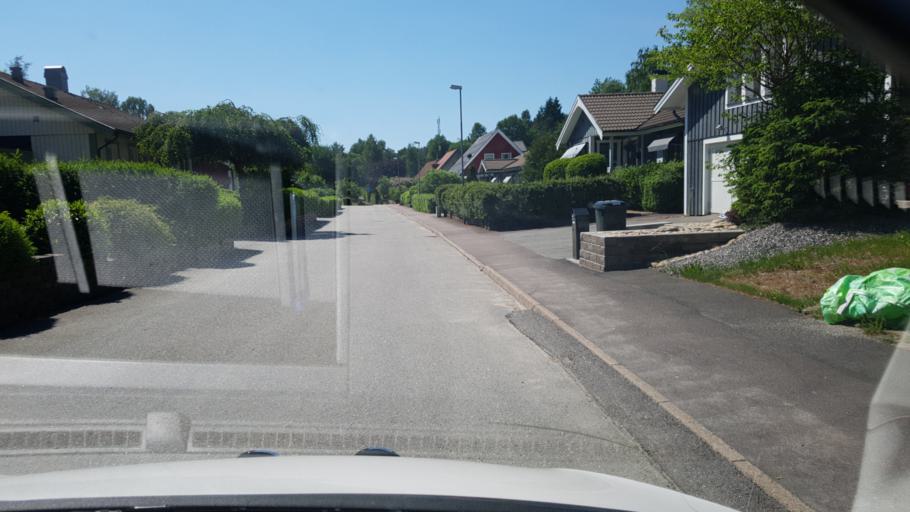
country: SE
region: Vaestra Goetaland
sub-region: Lerums Kommun
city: Stenkullen
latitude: 57.8003
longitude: 12.3591
